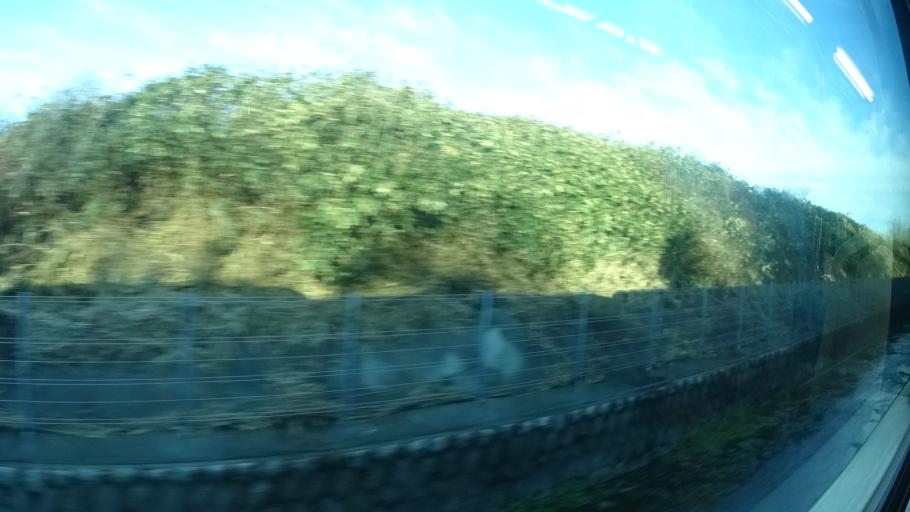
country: JP
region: Fukushima
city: Namie
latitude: 37.4014
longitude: 140.9855
